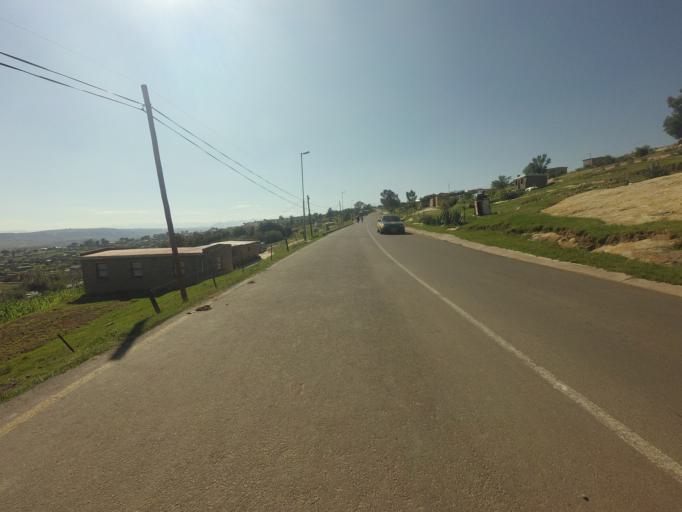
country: LS
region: Berea
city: Teyateyaneng
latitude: -29.1338
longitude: 27.7471
